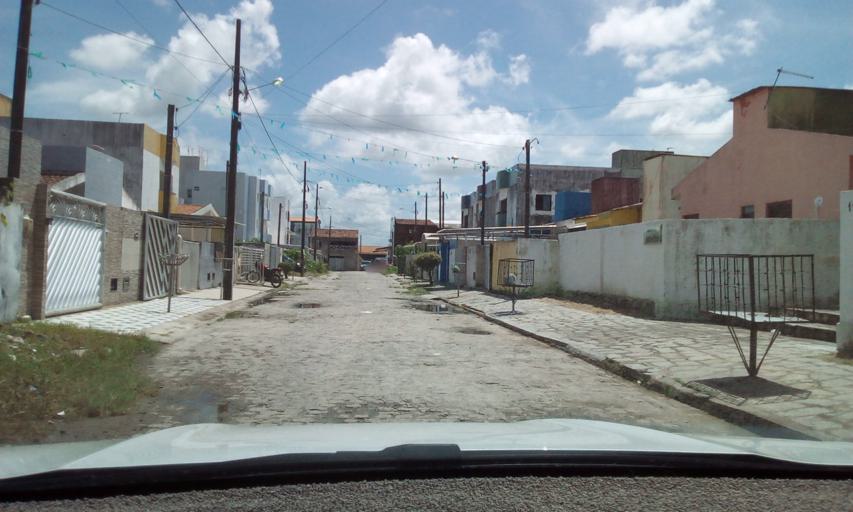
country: BR
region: Paraiba
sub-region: Bayeux
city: Bayeux
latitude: -7.1193
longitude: -34.9346
